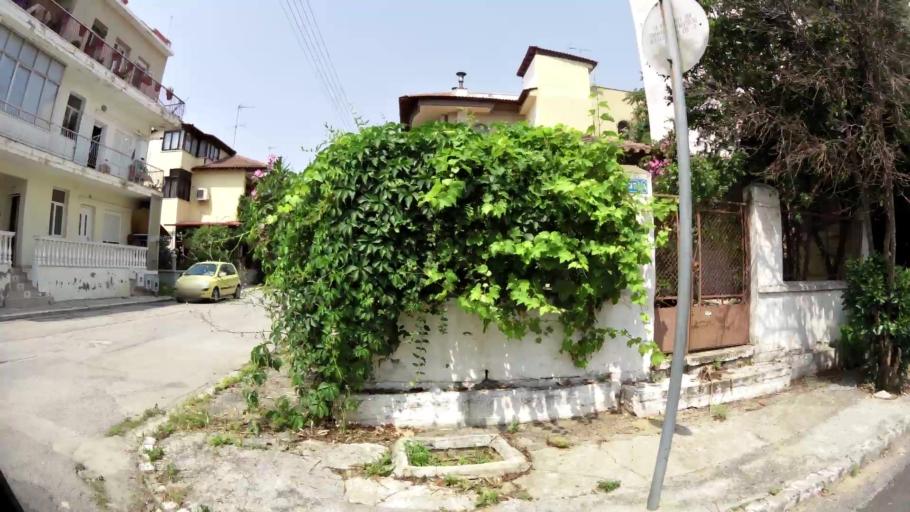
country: GR
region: Central Macedonia
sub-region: Nomos Thessalonikis
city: Diavata
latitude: 40.6851
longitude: 22.8611
